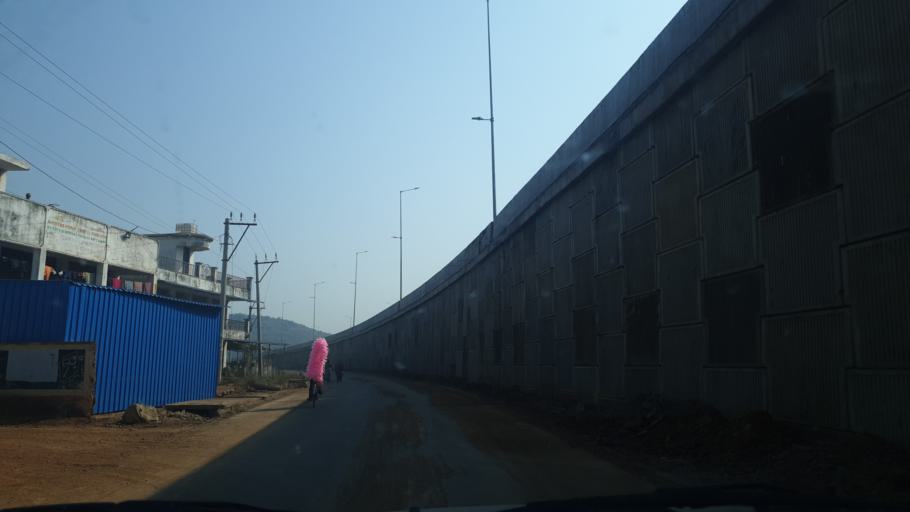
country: IN
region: Andhra Pradesh
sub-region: Srikakulam
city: Tekkali
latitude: 18.6194
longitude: 84.2437
